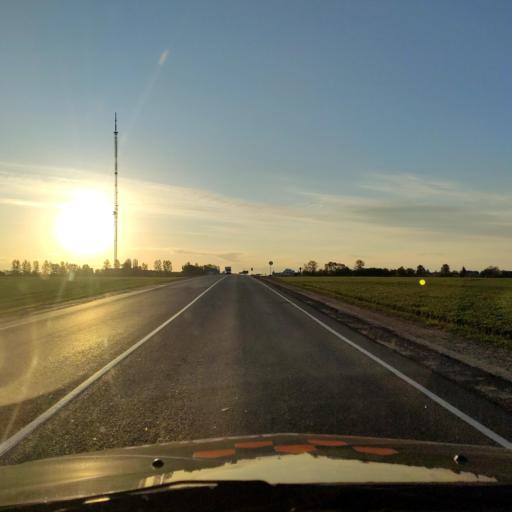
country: RU
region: Orjol
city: Livny
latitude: 52.4490
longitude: 37.4909
